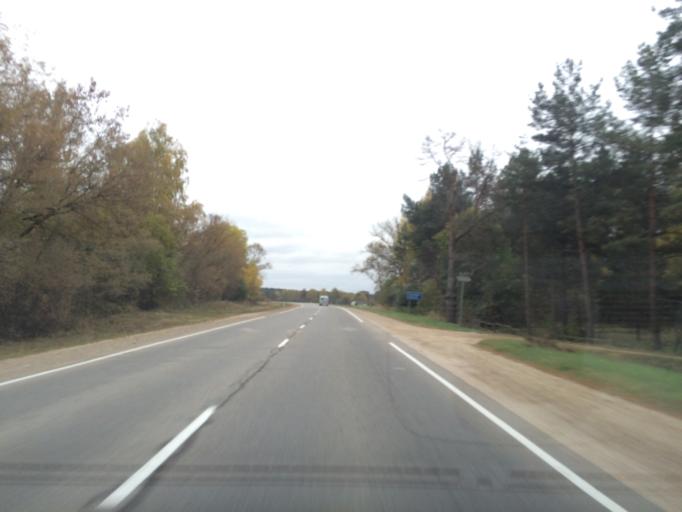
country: LV
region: Koknese
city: Koknese
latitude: 56.6089
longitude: 25.5040
